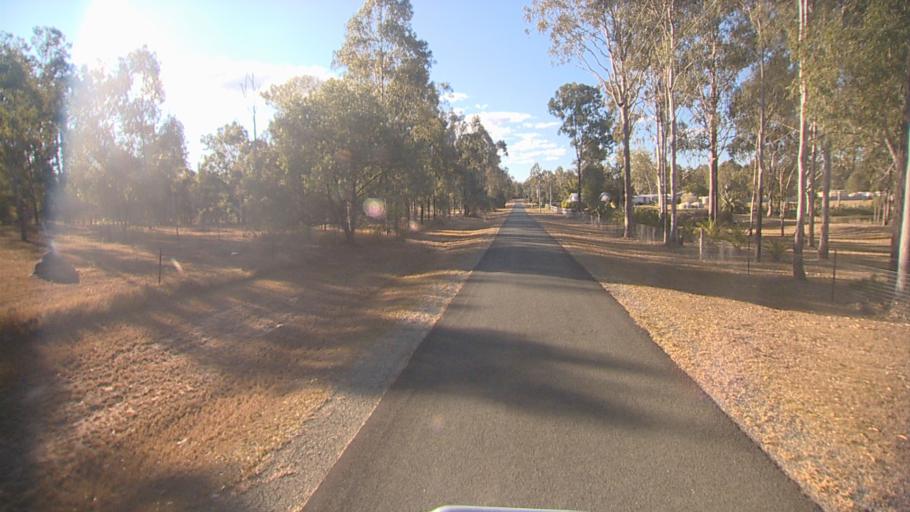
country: AU
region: Queensland
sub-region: Logan
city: Cedar Vale
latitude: -27.8462
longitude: 153.0133
